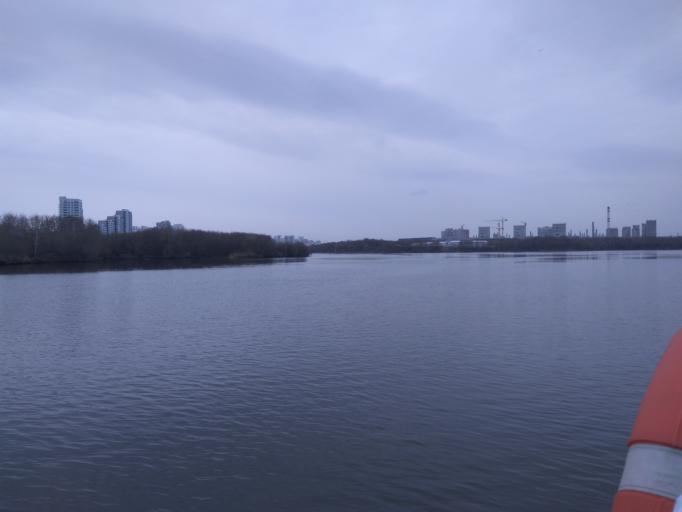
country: RU
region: Moskovskaya
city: Kozhukhovo
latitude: 55.6947
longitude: 37.6955
